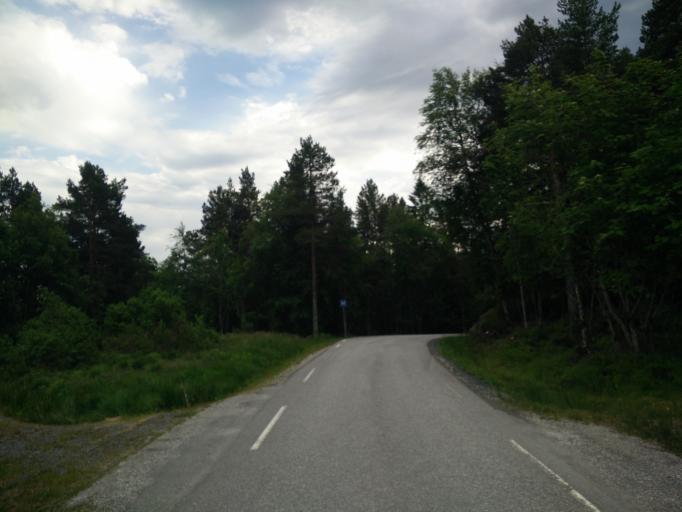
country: NO
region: More og Romsdal
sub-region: Kristiansund
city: Rensvik
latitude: 63.0346
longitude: 7.9553
